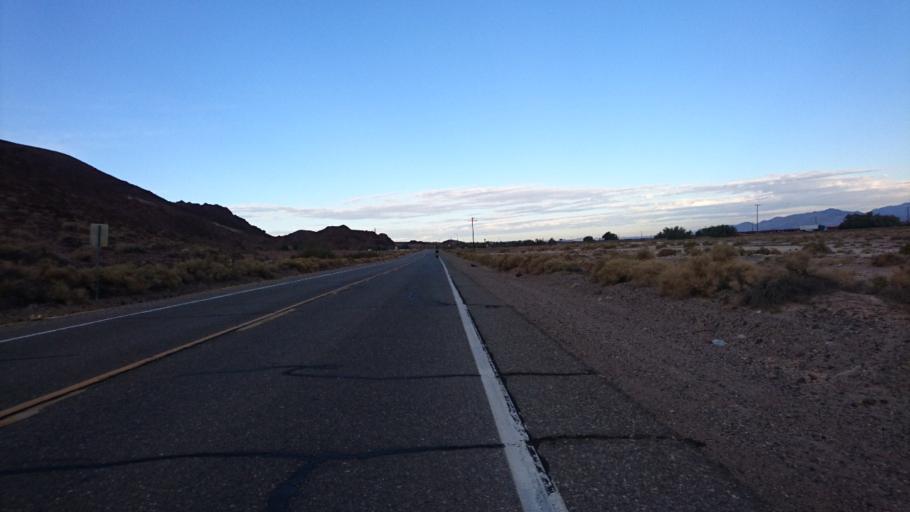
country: US
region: California
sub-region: San Bernardino County
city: Barstow
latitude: 34.8257
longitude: -116.6785
